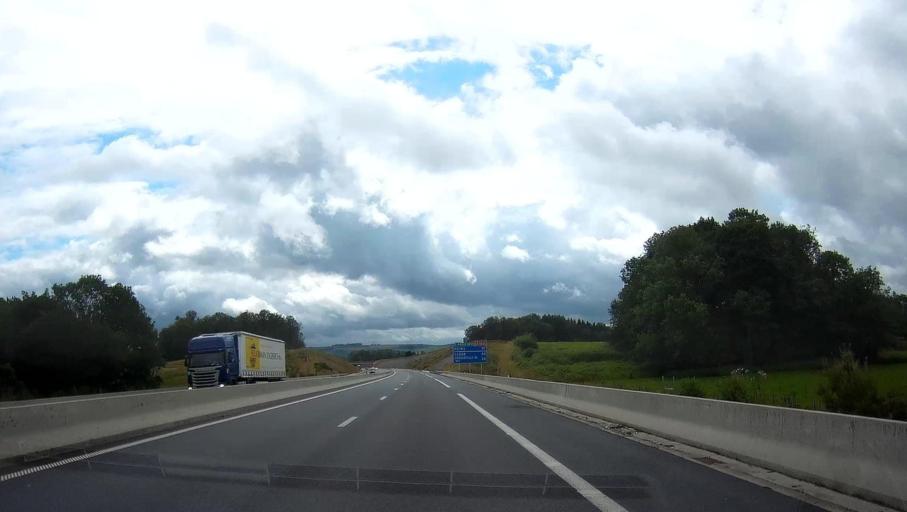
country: FR
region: Champagne-Ardenne
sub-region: Departement des Ardennes
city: Rimogne
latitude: 49.8299
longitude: 4.5114
